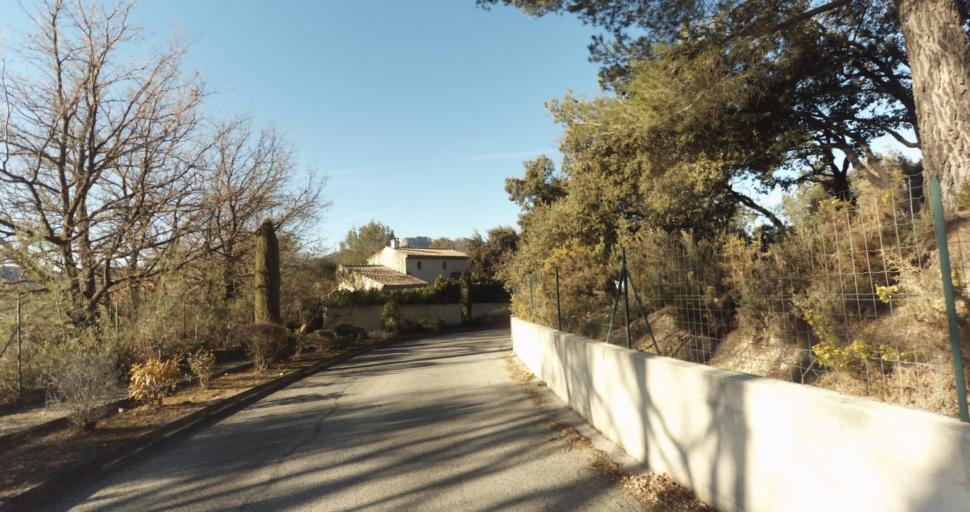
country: FR
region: Provence-Alpes-Cote d'Azur
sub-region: Departement des Bouches-du-Rhone
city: Peypin
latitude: 43.4033
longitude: 5.5720
